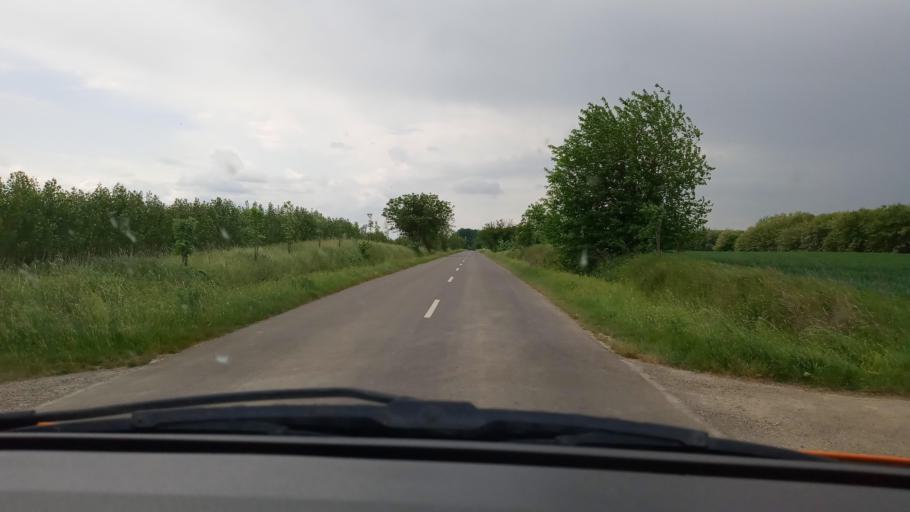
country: HU
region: Baranya
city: Vajszlo
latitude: 45.8510
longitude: 17.9808
